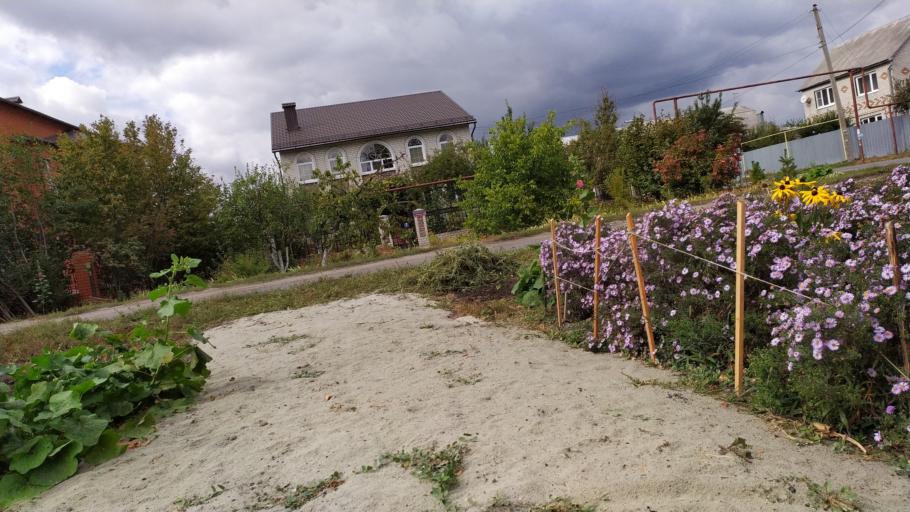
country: RU
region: Kursk
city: Kursk
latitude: 51.6419
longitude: 36.1392
